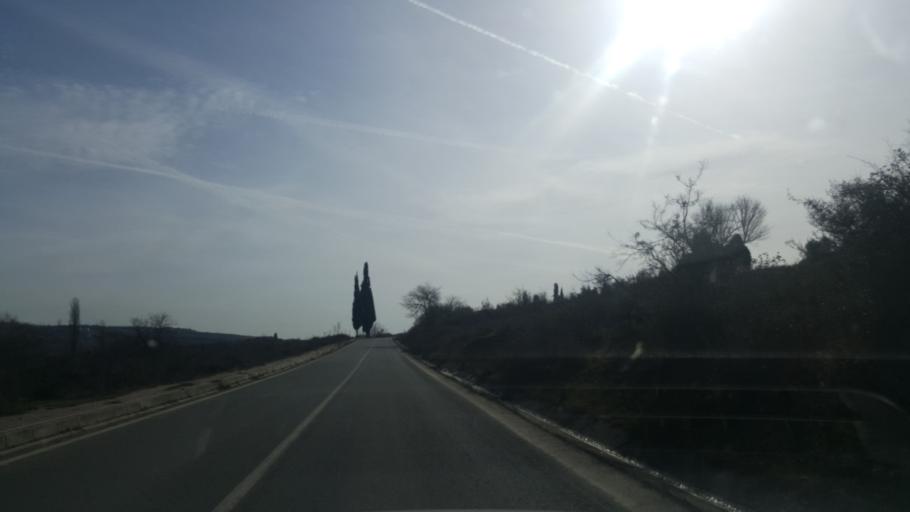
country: TR
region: Kocaeli
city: Tavsancil
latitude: 40.7890
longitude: 29.5685
